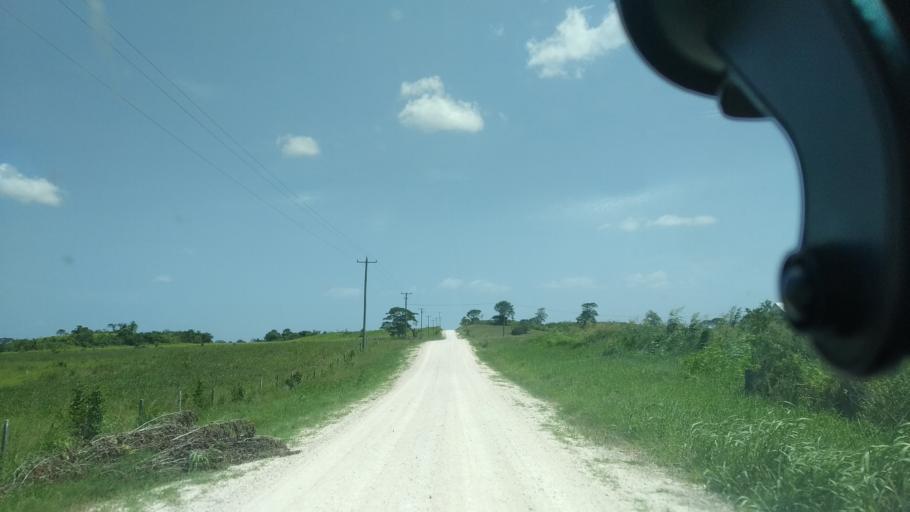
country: BZ
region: Cayo
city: San Ignacio
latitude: 17.3095
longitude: -89.0480
